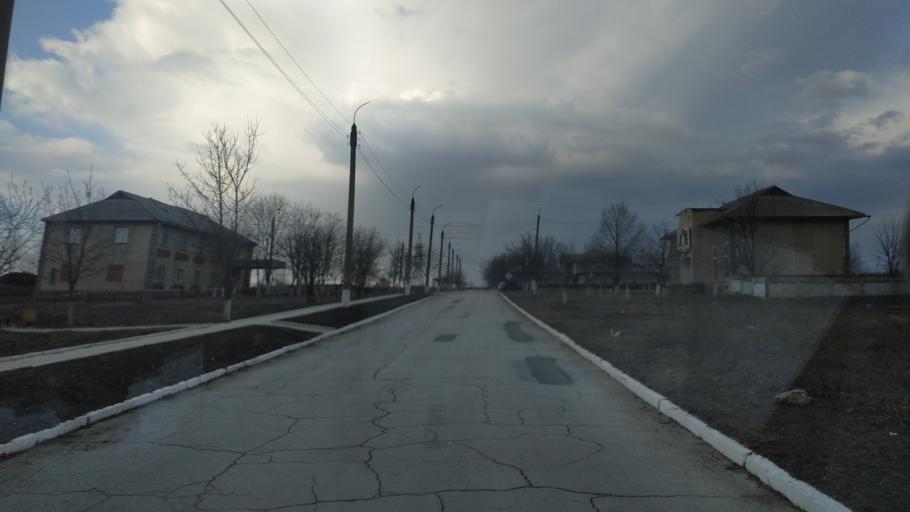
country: MD
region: Telenesti
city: Grigoriopol
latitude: 47.0112
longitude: 29.2950
